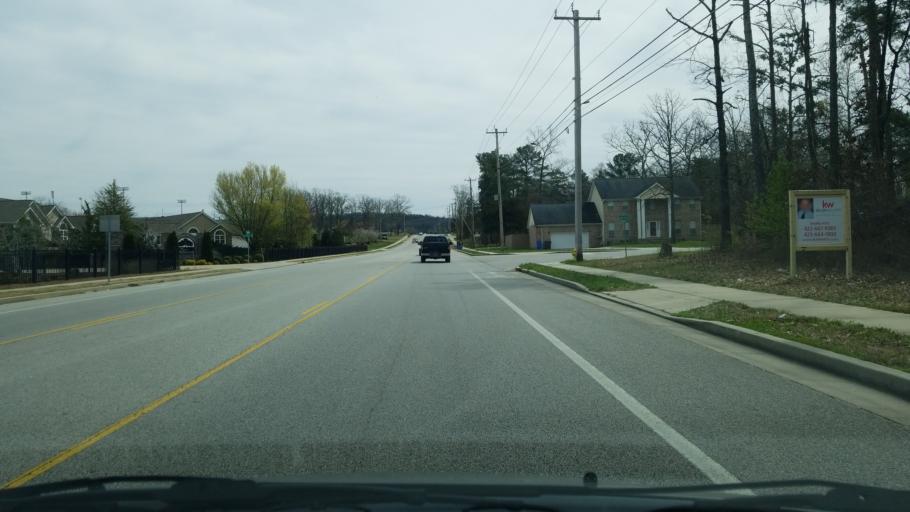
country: US
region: Tennessee
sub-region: Hamilton County
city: East Brainerd
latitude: 35.0364
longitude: -85.1395
